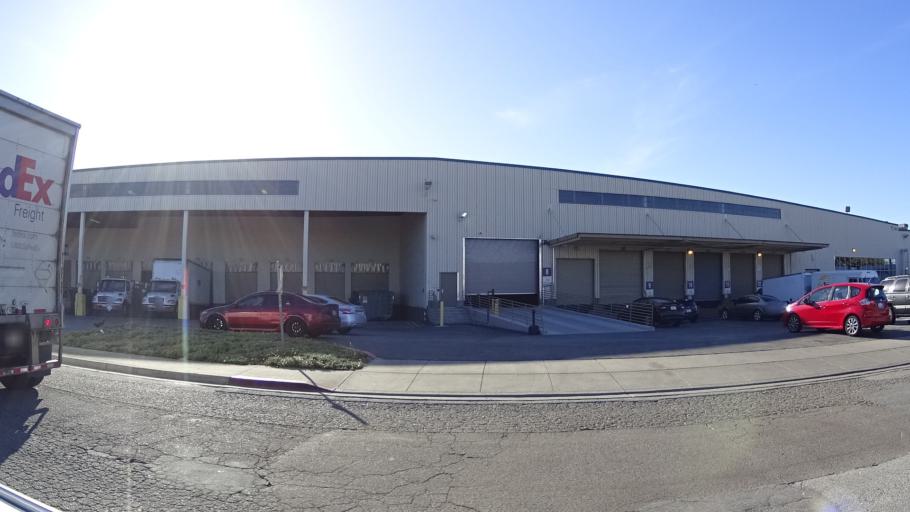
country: US
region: California
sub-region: San Mateo County
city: South San Francisco
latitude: 37.6459
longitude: -122.3953
